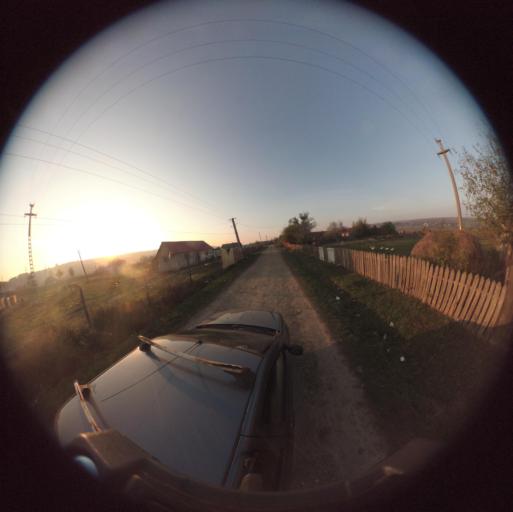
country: RO
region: Vaslui
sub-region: Comuna Bacesti
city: Bacesti
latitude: 46.8310
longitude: 27.2470
